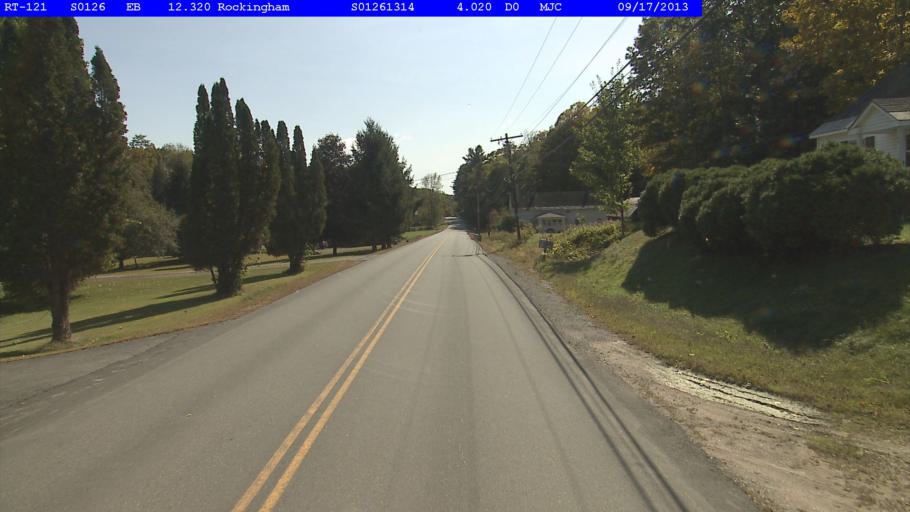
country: US
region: Vermont
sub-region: Windham County
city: Bellows Falls
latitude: 43.1389
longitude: -72.4908
